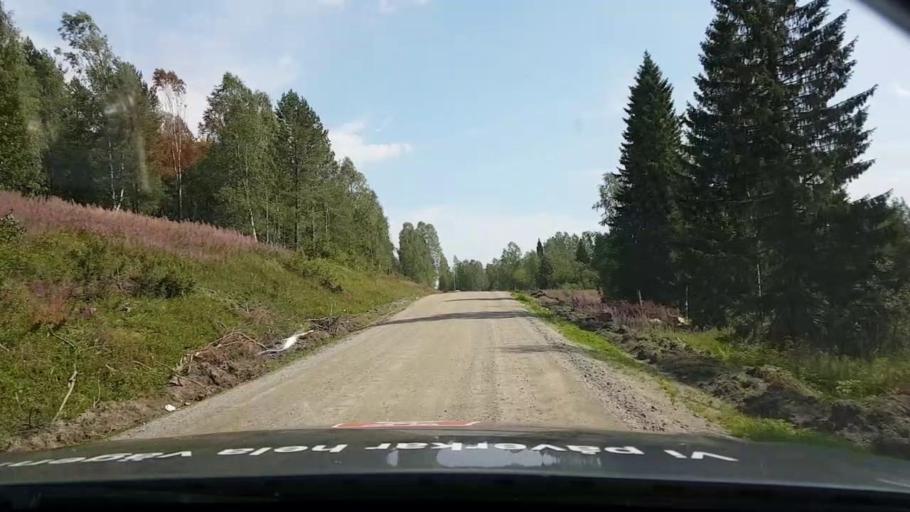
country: SE
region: Jaemtland
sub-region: Braecke Kommun
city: Braecke
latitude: 62.7256
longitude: 15.5323
